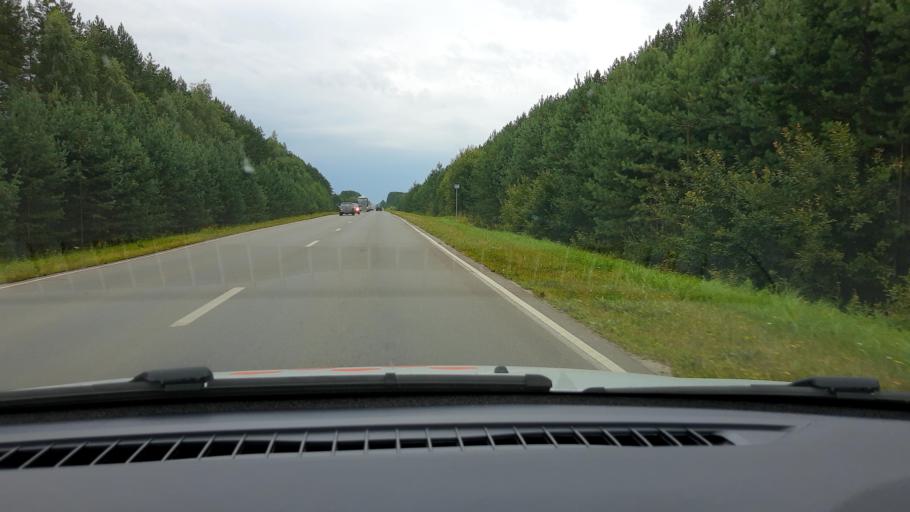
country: RU
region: Nizjnij Novgorod
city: Vyyezdnoye
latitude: 55.1654
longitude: 43.5885
